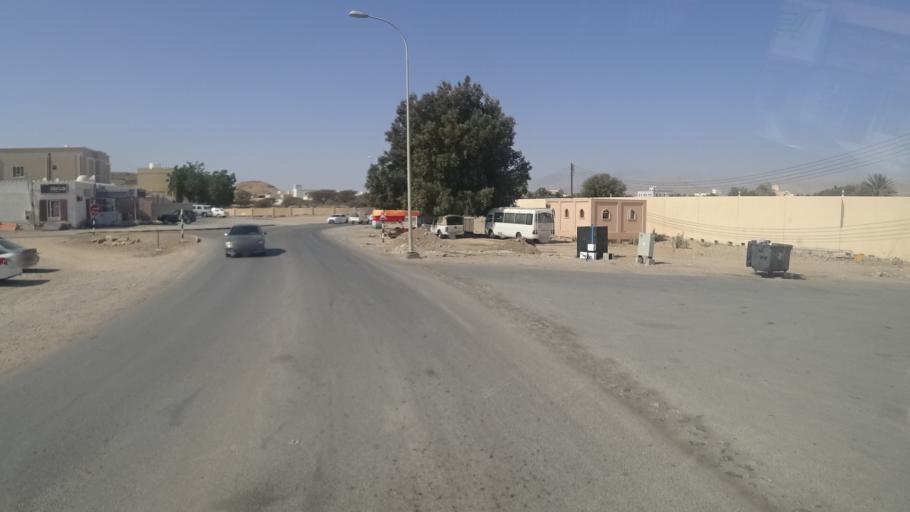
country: OM
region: Ash Sharqiyah
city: Sur
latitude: 22.5398
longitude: 59.4891
